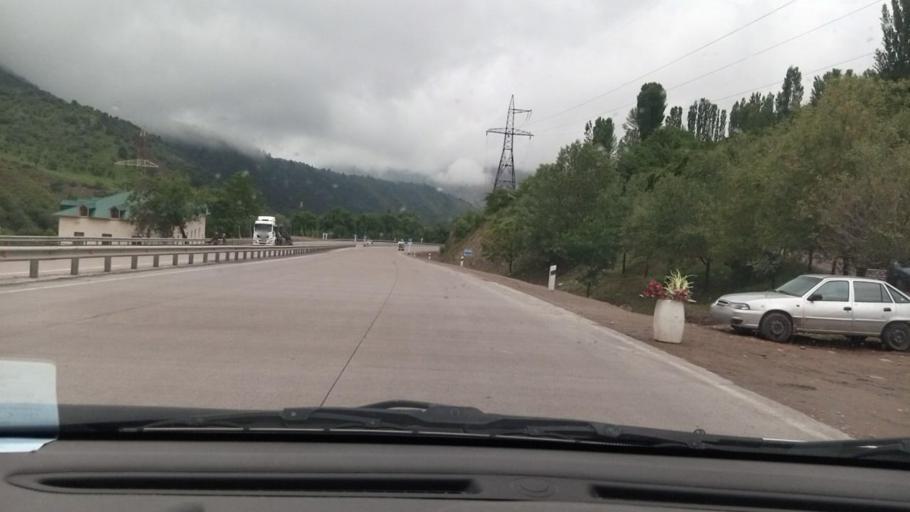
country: UZ
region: Toshkent
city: Angren
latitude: 41.1328
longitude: 70.4646
